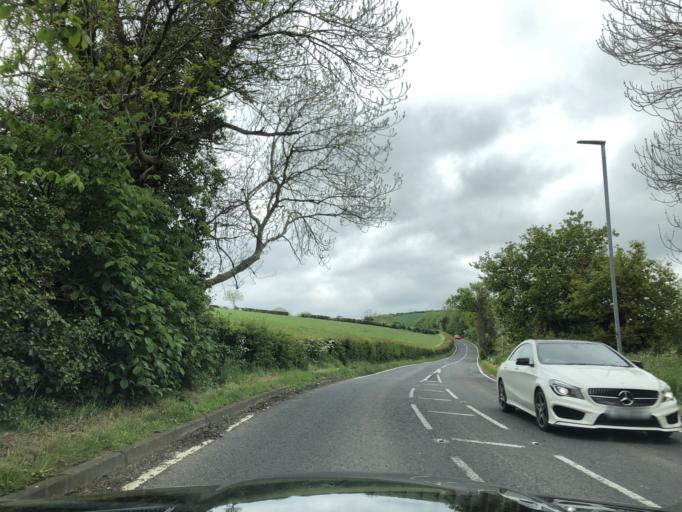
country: GB
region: Northern Ireland
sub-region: Down District
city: Downpatrick
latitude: 54.3542
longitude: -5.7401
